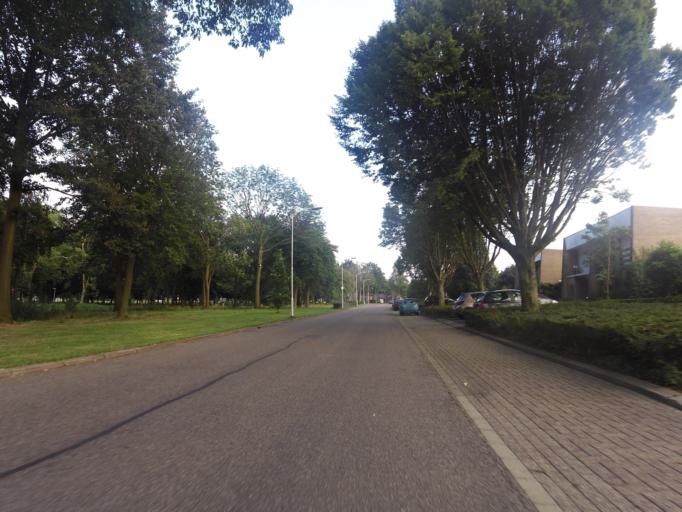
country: NL
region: Gelderland
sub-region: Oude IJsselstreek
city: Gendringen
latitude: 51.8763
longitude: 6.3815
